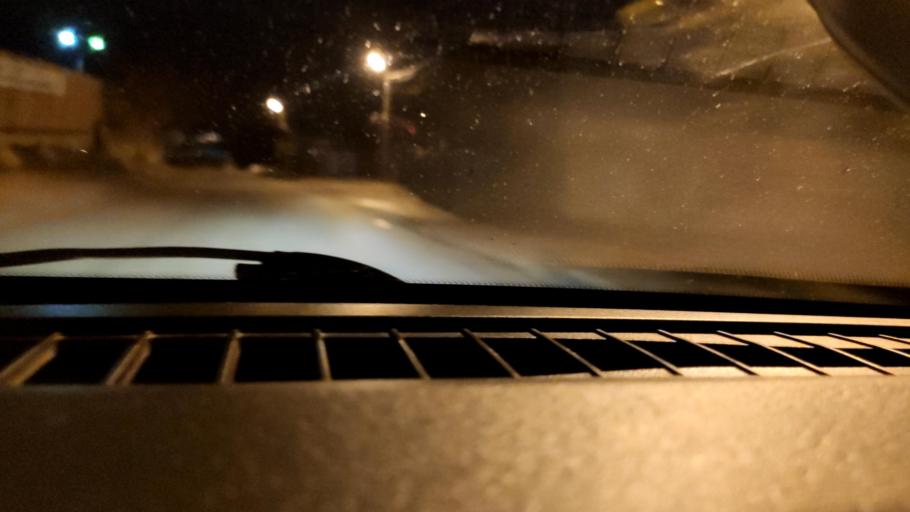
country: RU
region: Samara
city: Samara
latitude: 53.1795
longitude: 50.1567
